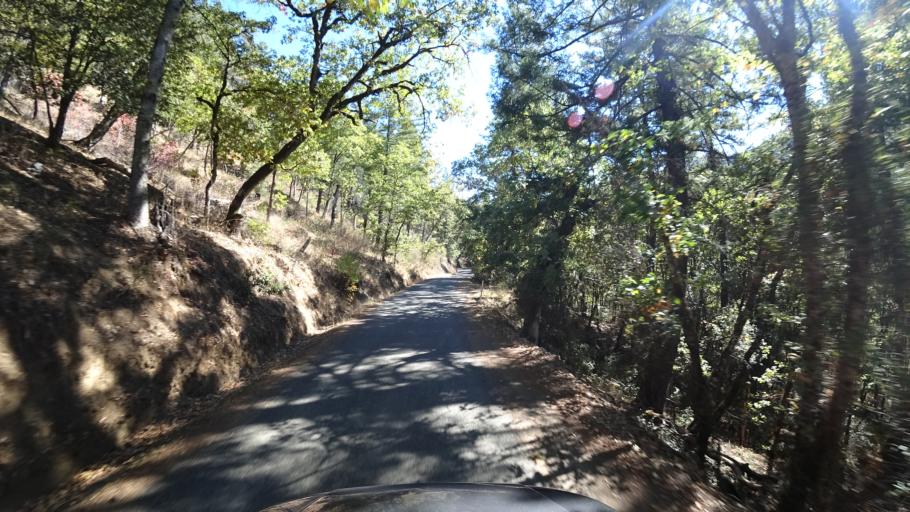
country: US
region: California
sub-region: Humboldt County
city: Willow Creek
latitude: 41.2807
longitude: -123.3500
